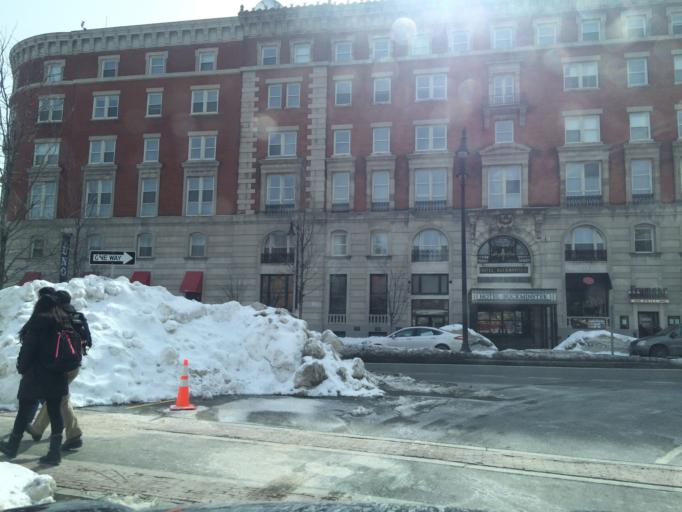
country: US
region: Massachusetts
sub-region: Middlesex County
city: Cambridge
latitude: 42.3488
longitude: -71.0979
